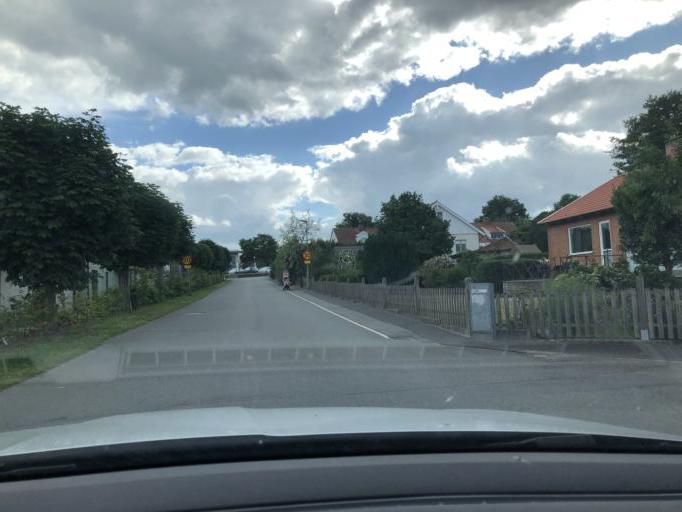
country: SE
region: Skane
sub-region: Simrishamns Kommun
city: Kivik
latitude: 55.6852
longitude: 14.2302
